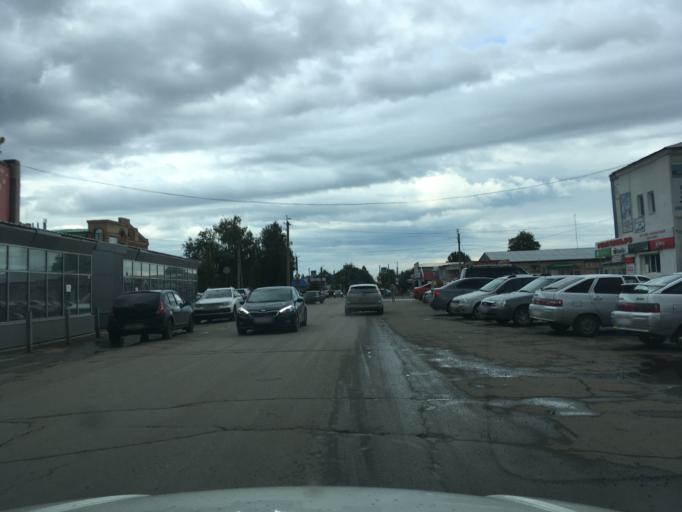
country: RU
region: Samara
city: Bezenchuk
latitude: 52.9800
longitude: 49.4318
